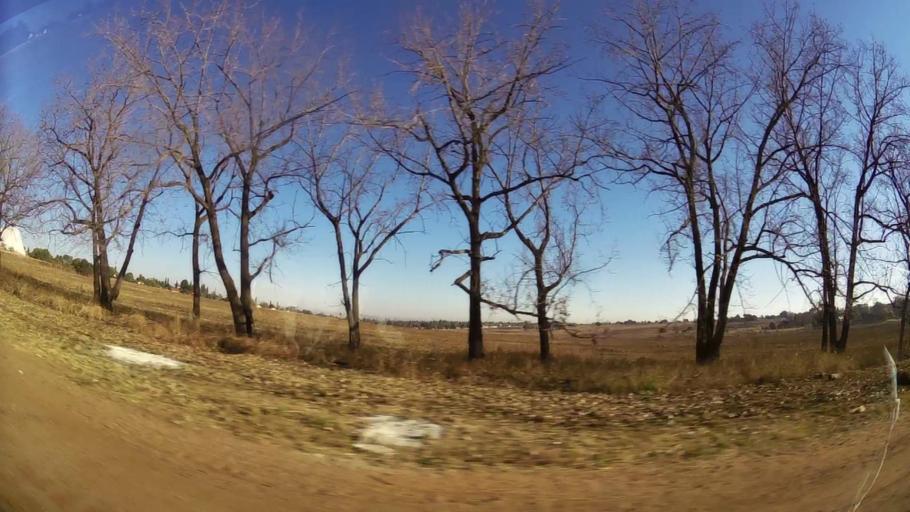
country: ZA
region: Gauteng
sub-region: Ekurhuleni Metropolitan Municipality
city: Tembisa
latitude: -26.0450
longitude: 28.2445
